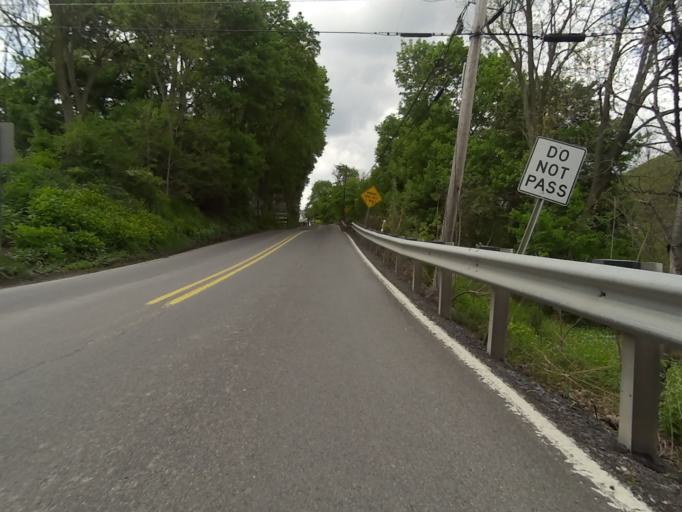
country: US
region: Pennsylvania
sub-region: Centre County
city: Boalsburg
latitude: 40.7934
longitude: -77.7999
